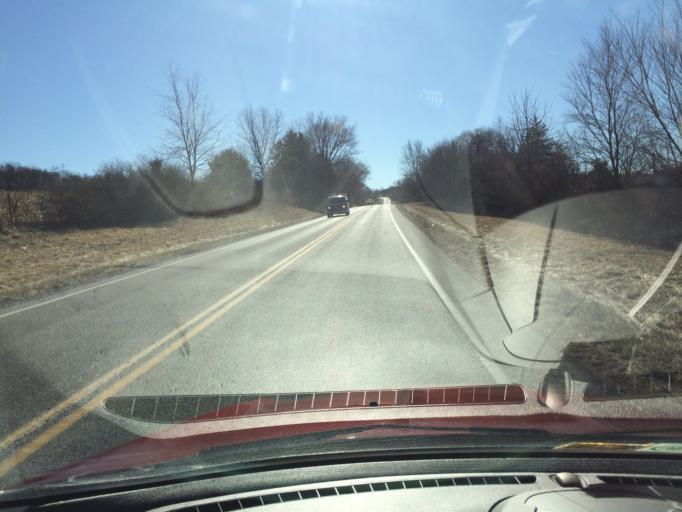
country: US
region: Virginia
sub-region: Augusta County
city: Weyers Cave
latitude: 38.2995
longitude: -78.9343
